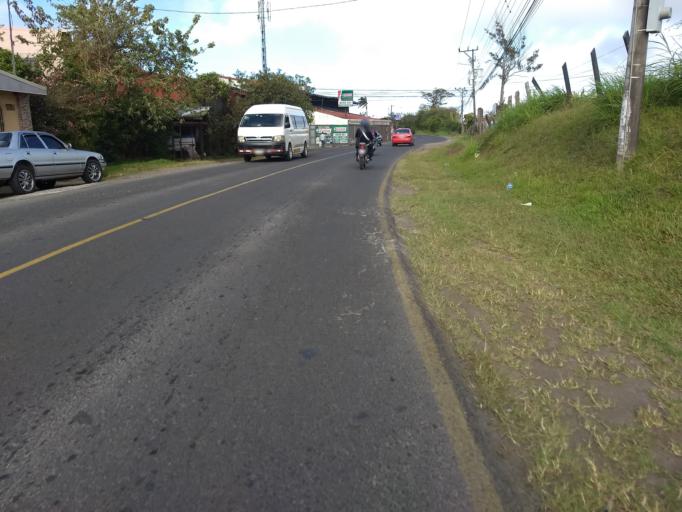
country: CR
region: San Jose
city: San Vicente de Moravia
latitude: 9.9665
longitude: -84.0425
